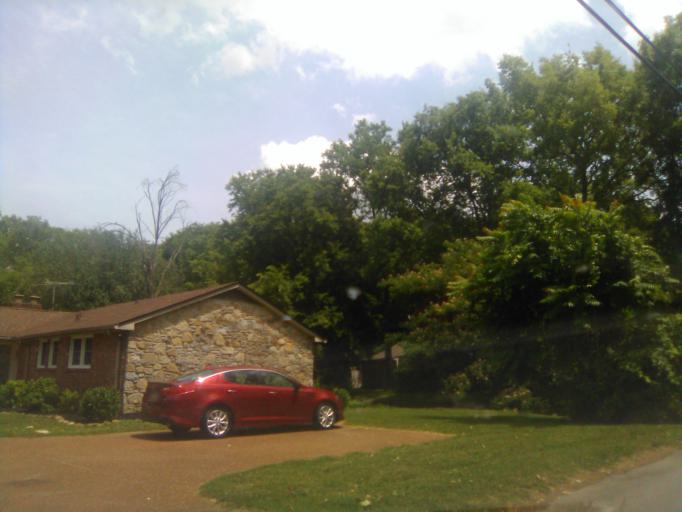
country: US
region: Tennessee
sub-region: Davidson County
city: Belle Meade
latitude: 36.0956
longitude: -86.8770
